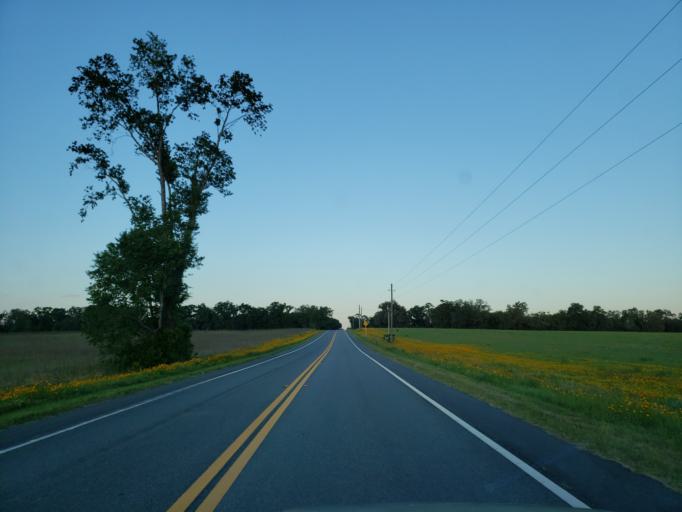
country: US
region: Florida
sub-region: Madison County
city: Madison
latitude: 30.5813
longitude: -83.2365
